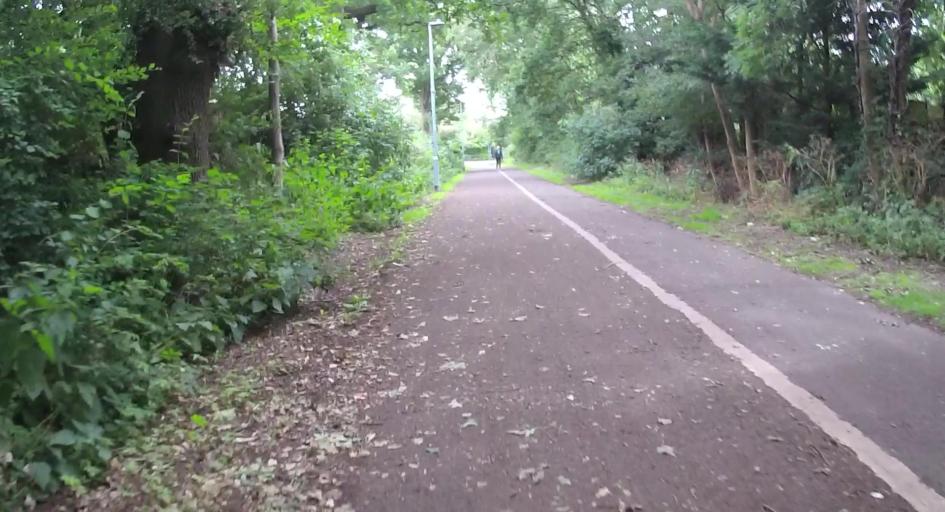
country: GB
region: England
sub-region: Wokingham
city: Lower Earley
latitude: 51.4243
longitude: -0.9259
